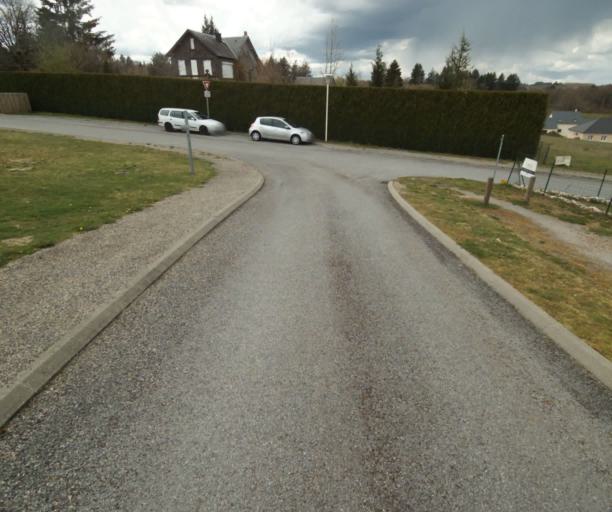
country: FR
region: Limousin
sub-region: Departement de la Correze
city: Correze
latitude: 45.3355
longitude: 1.9448
